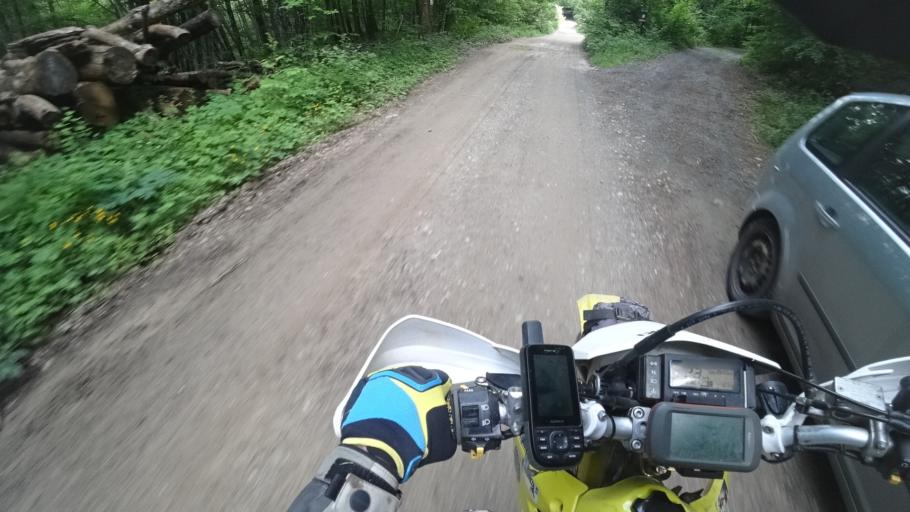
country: HR
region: Licko-Senjska
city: Gospic
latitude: 44.4810
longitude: 15.3113
